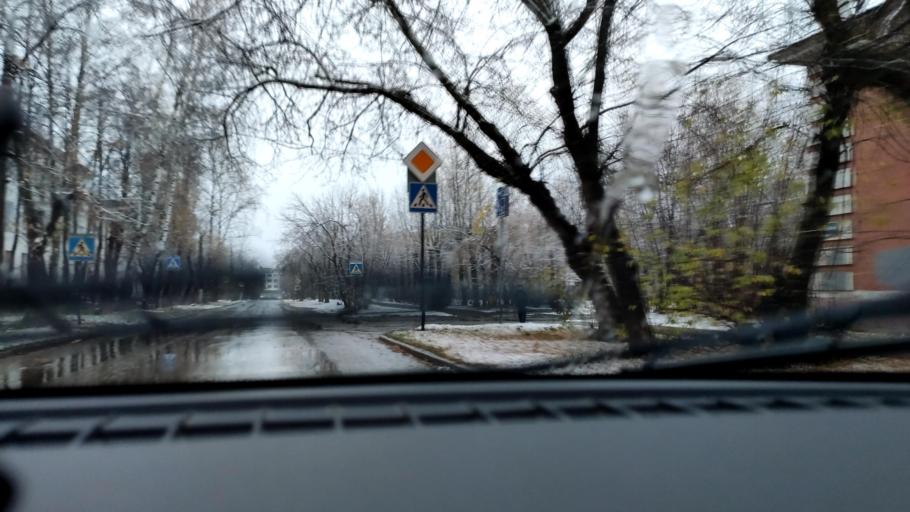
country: RU
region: Perm
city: Kultayevo
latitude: 57.9978
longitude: 55.9427
